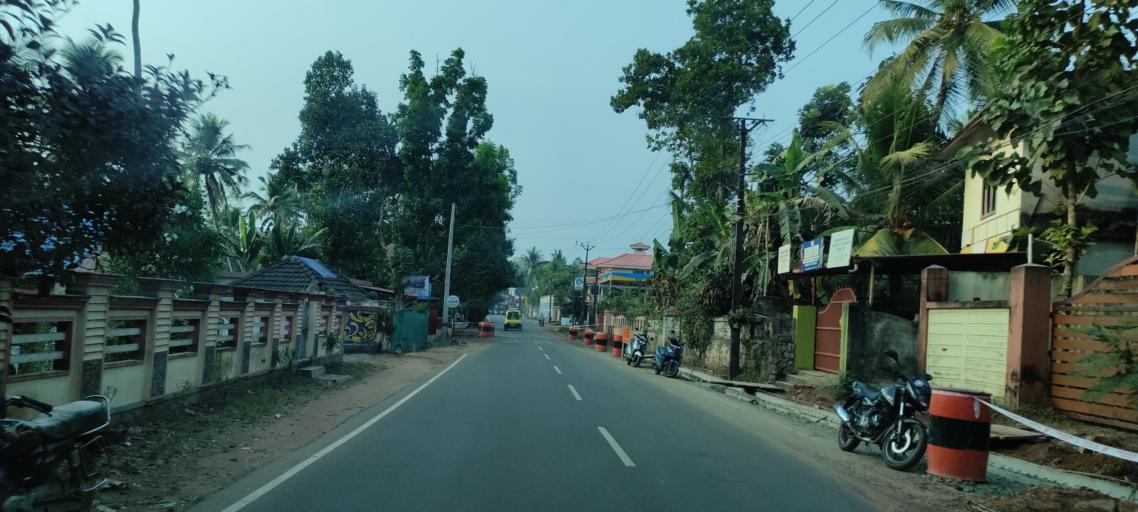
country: IN
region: Kerala
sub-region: Alappuzha
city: Mavelikara
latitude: 9.2527
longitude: 76.5673
